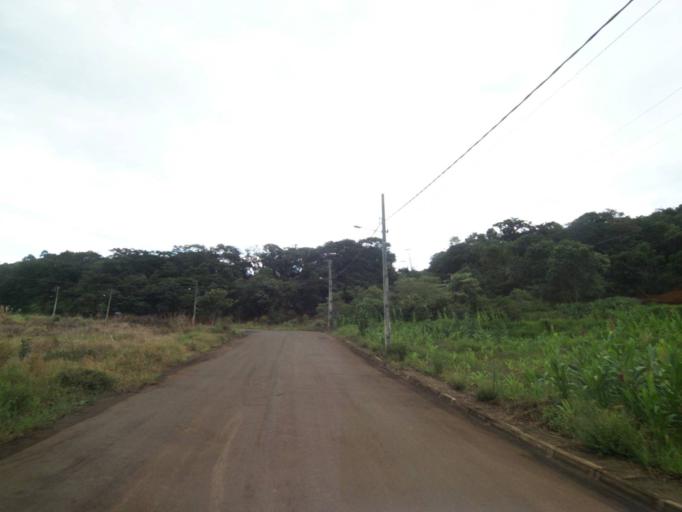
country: BR
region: Parana
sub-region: Guaraniacu
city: Guaraniacu
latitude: -25.0989
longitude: -52.8855
